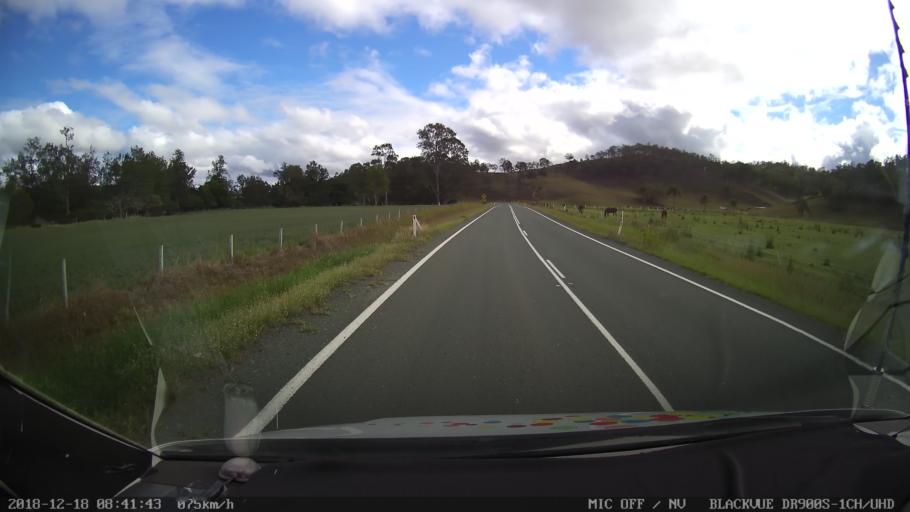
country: AU
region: Queensland
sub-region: Logan
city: Cedar Vale
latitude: -28.2337
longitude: 152.8591
